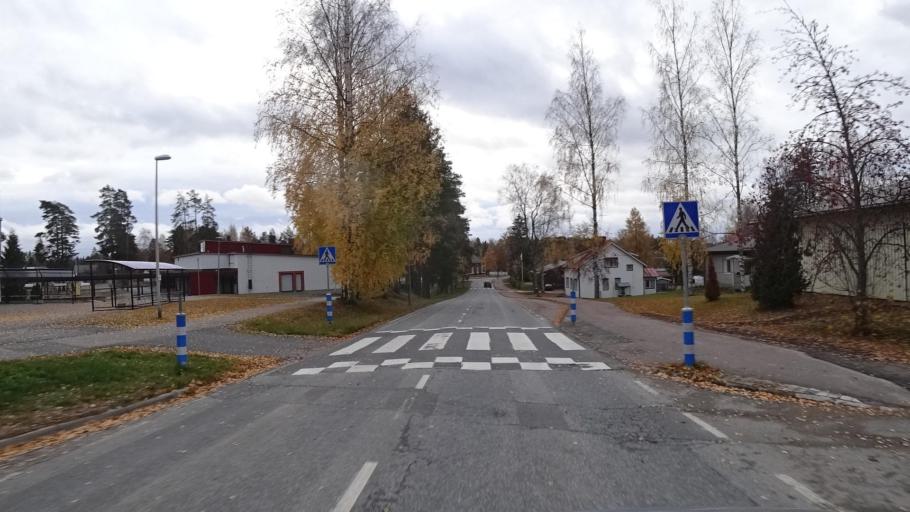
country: FI
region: Central Finland
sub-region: Joutsa
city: Joutsa
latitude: 61.7468
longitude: 26.1210
